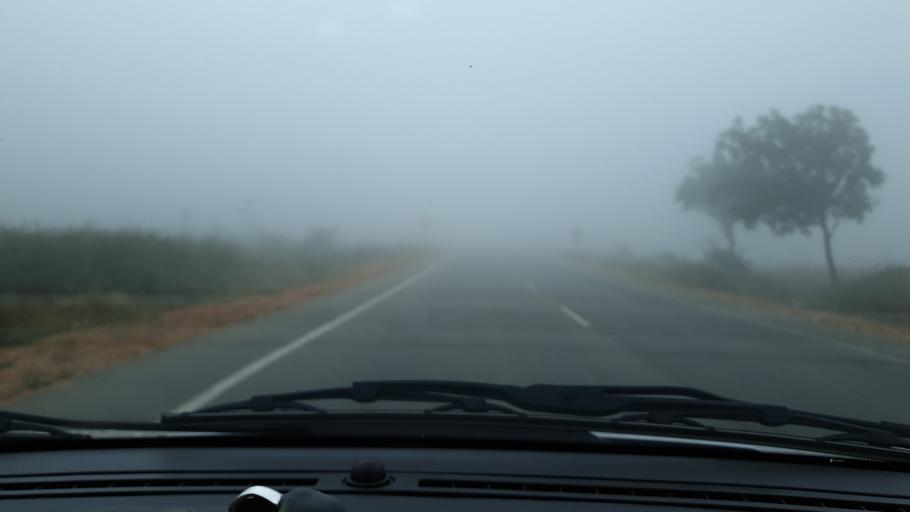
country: IN
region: Telangana
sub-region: Mahbubnagar
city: Nagar Karnul
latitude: 16.6745
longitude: 78.5302
